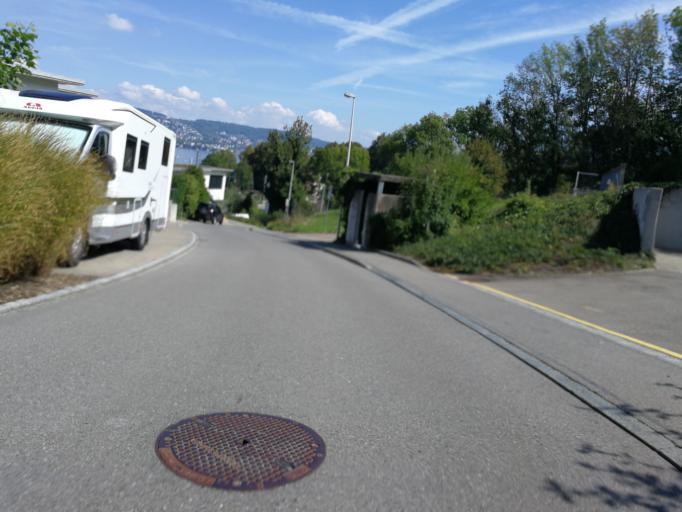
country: CH
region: Zurich
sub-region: Bezirk Horgen
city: Au / Unter-Dorf
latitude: 47.2506
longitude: 8.6263
